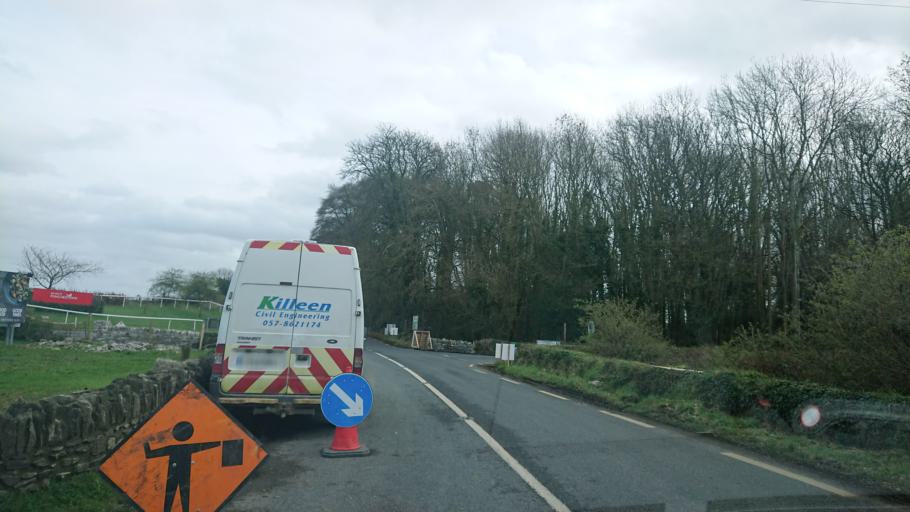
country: IE
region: Leinster
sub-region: Kildare
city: Naas
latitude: 53.1875
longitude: -6.6424
